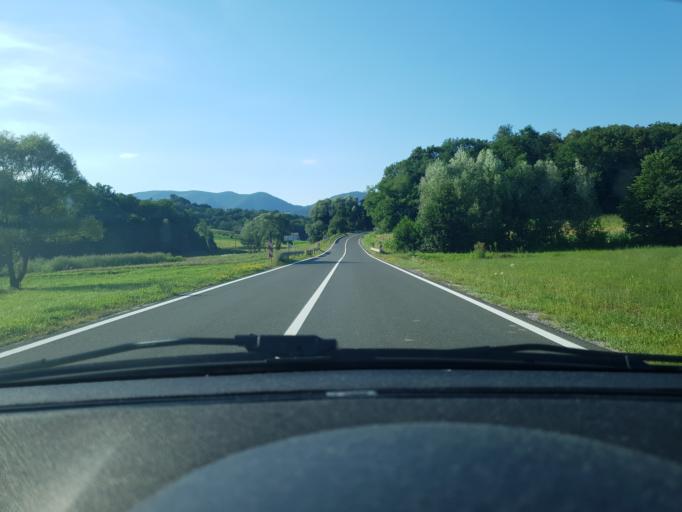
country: HR
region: Krapinsko-Zagorska
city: Radoboj
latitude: 46.1427
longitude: 15.9400
